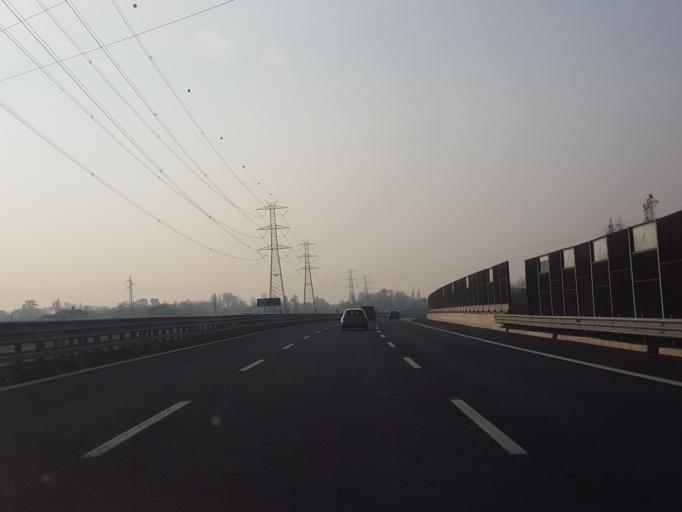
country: IT
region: Veneto
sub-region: Provincia di Treviso
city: Preganziol
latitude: 45.5880
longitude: 12.2430
